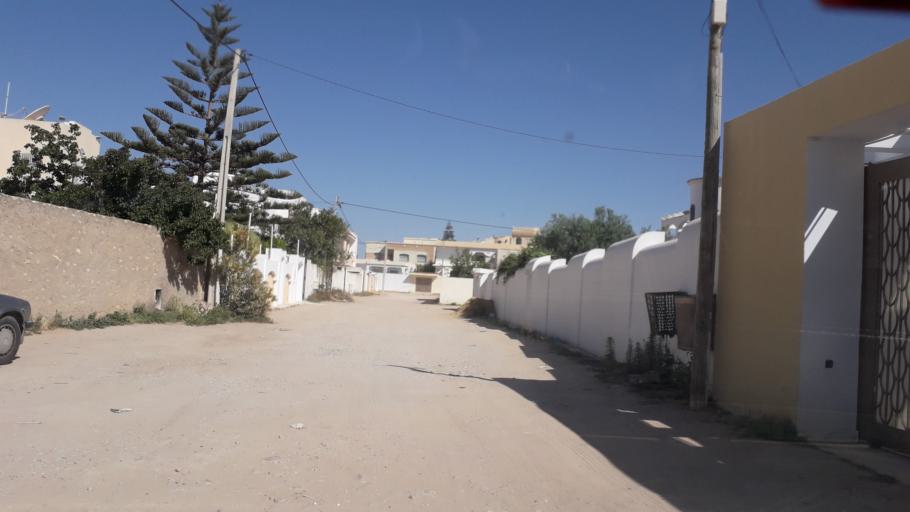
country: TN
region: Safaqis
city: Al Qarmadah
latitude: 34.8070
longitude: 10.7657
